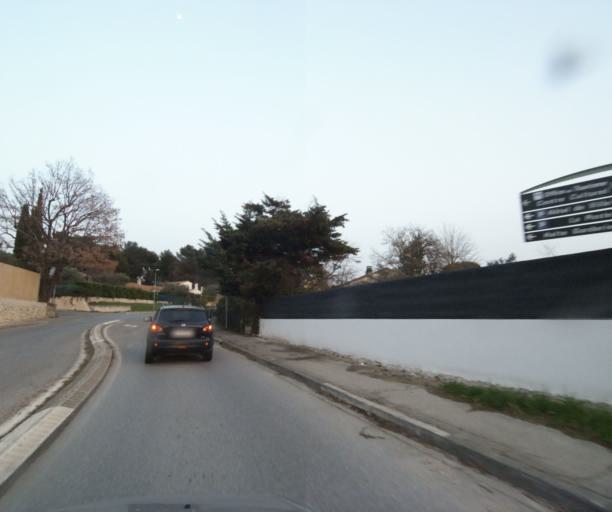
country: FR
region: Provence-Alpes-Cote d'Azur
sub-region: Departement des Bouches-du-Rhone
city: Simiane-Collongue
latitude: 43.4341
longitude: 5.4287
